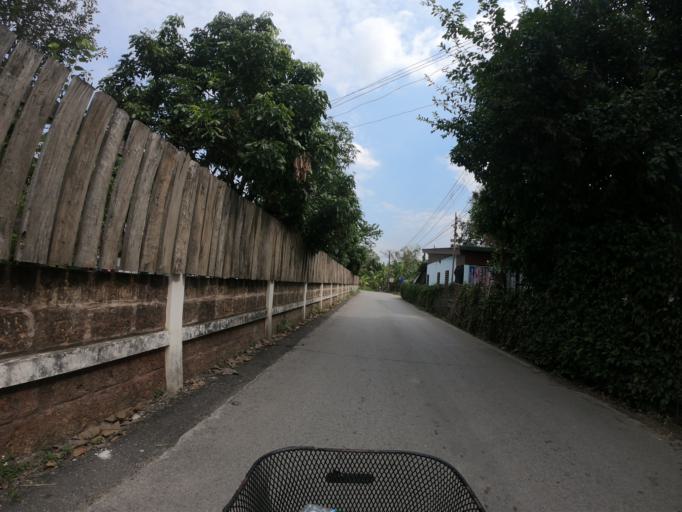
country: TH
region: Chiang Mai
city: Saraphi
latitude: 18.7082
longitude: 99.0353
